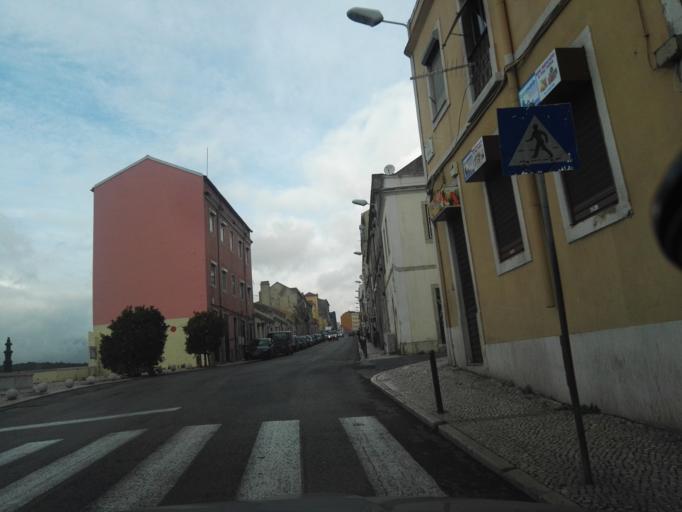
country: PT
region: Setubal
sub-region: Almada
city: Cacilhas
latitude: 38.7160
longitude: -9.1727
